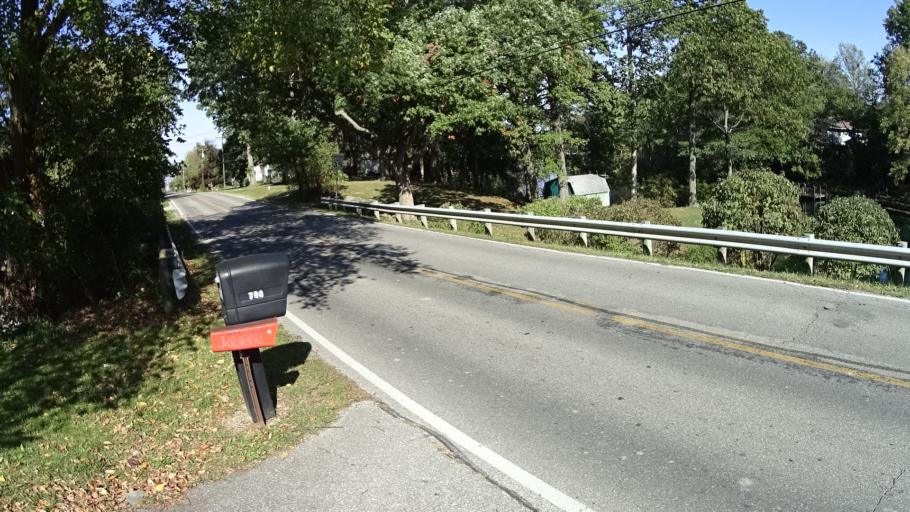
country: US
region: Ohio
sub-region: Lorain County
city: Vermilion-on-the-Lake
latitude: 41.4195
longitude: -82.3045
